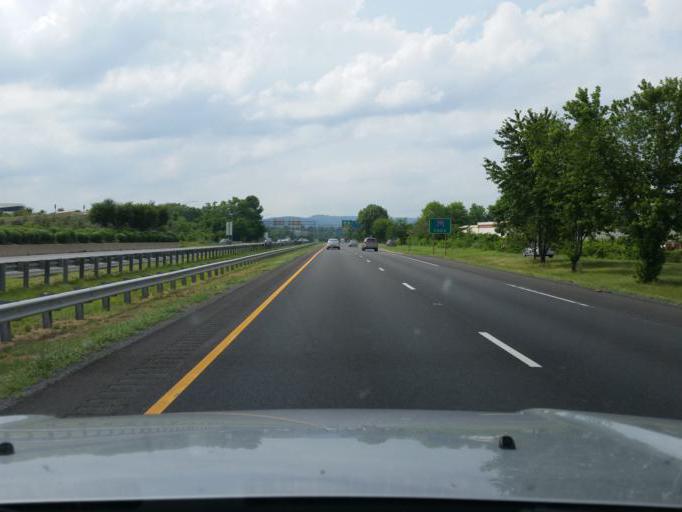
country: US
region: Maryland
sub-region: Frederick County
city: Frederick
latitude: 39.3999
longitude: -77.4262
